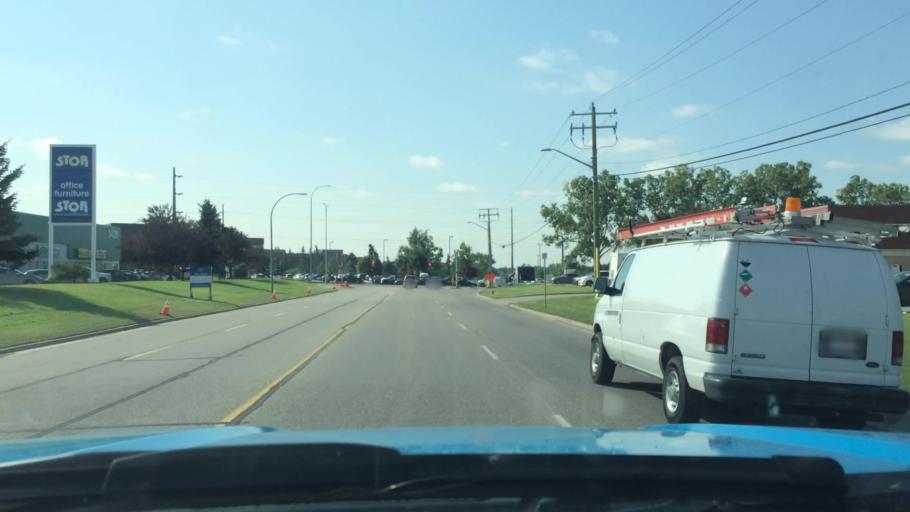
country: CA
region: Alberta
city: Calgary
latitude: 51.0829
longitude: -114.0297
